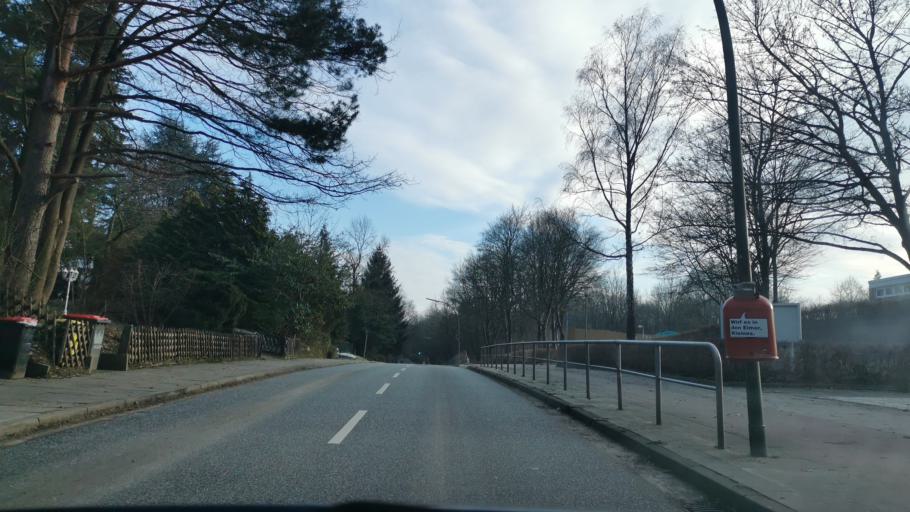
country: DE
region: Lower Saxony
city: Seevetal
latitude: 53.4313
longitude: 9.9703
